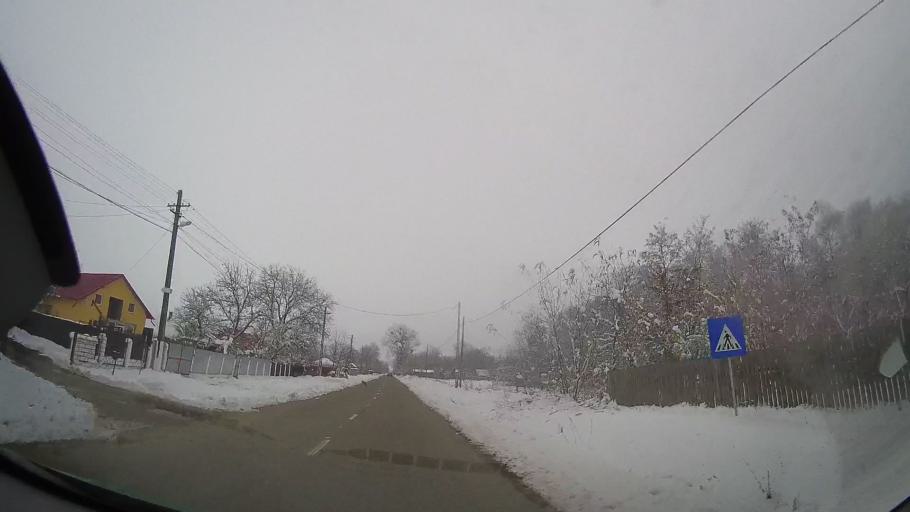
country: RO
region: Neamt
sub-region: Comuna Bozieni
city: Bozieni
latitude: 46.8326
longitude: 27.1648
